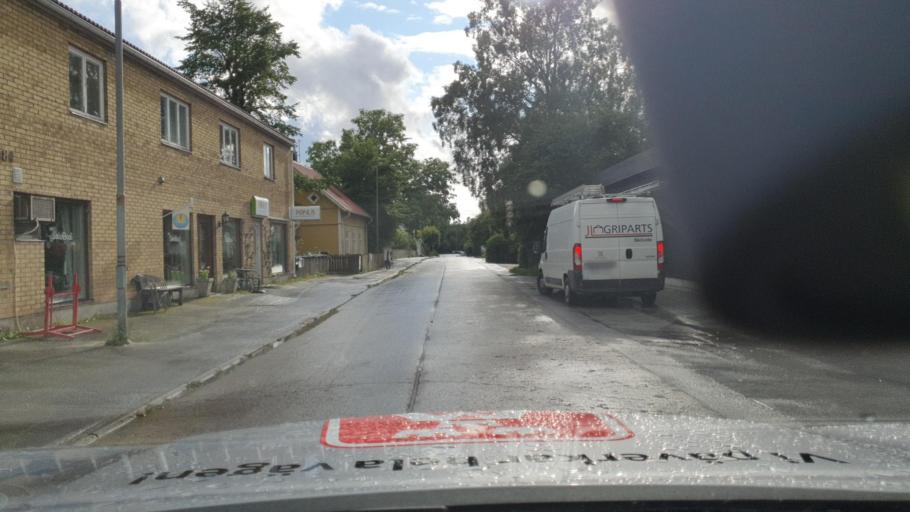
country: SE
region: Gotland
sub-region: Gotland
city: Slite
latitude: 57.7042
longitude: 18.8040
